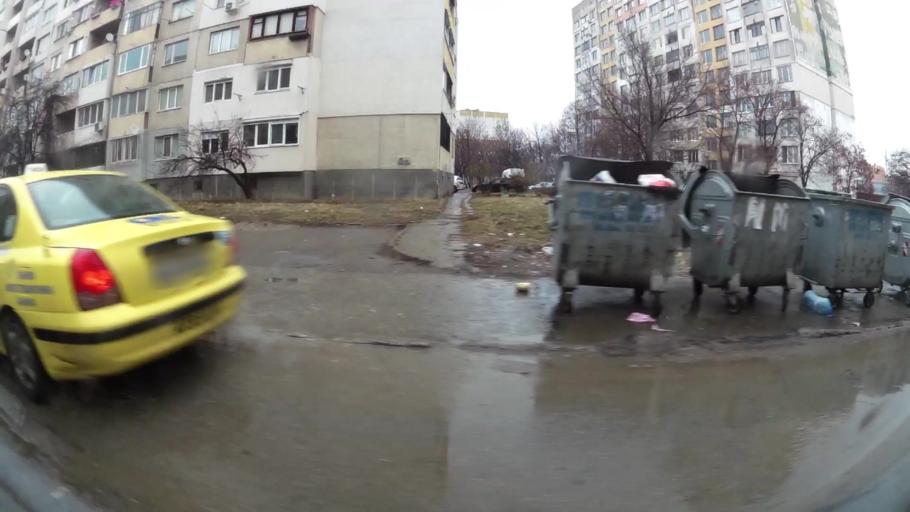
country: BG
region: Sofia-Capital
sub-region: Stolichna Obshtina
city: Sofia
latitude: 42.6660
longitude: 23.3902
